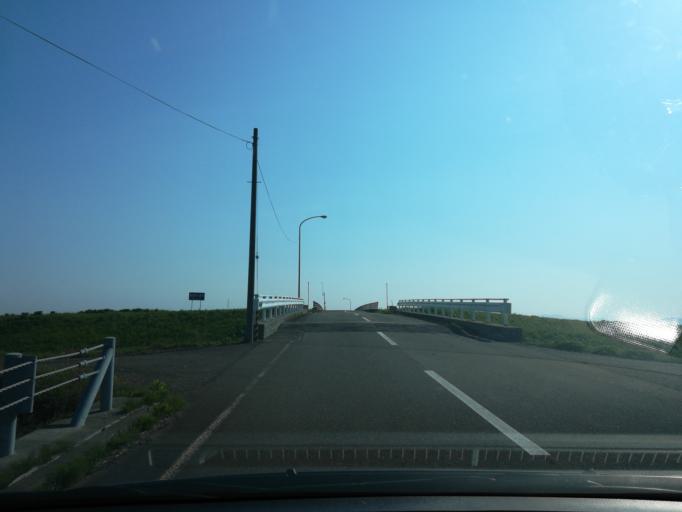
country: JP
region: Hokkaido
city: Iwamizawa
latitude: 43.1317
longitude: 141.6774
